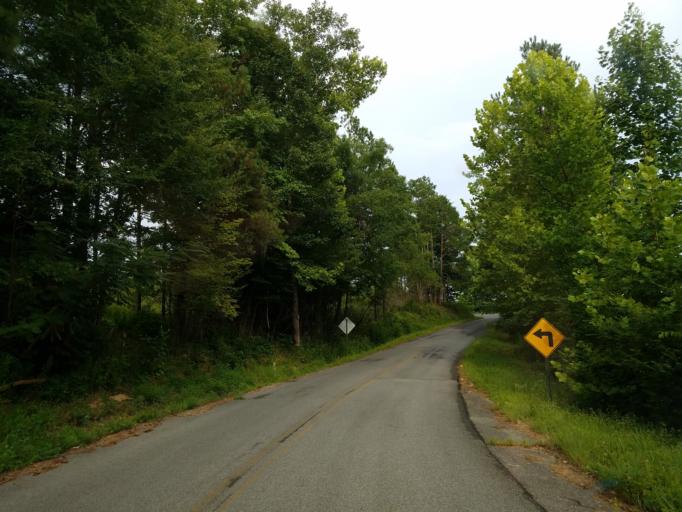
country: US
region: Georgia
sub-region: Bartow County
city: Rydal
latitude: 34.3905
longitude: -84.6684
